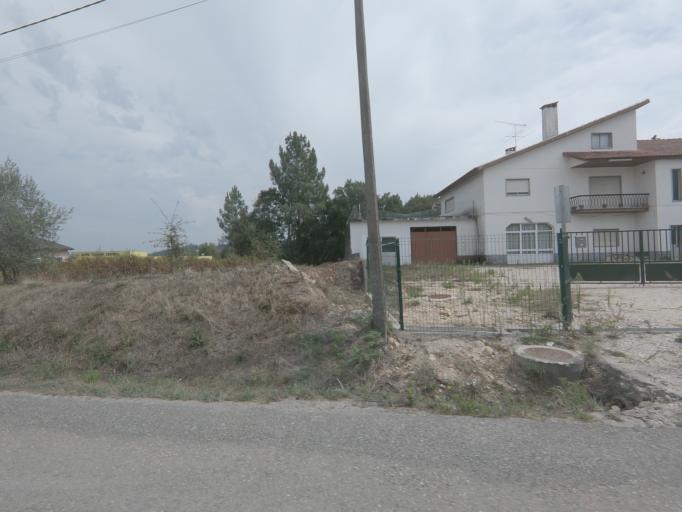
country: PT
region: Leiria
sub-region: Pombal
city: Pombal
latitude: 39.8960
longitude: -8.6526
